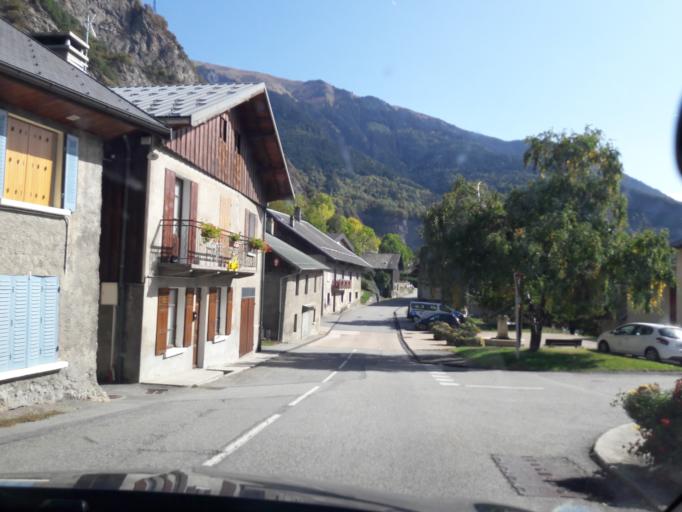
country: FR
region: Rhone-Alpes
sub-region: Departement de la Savoie
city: Saint-Jean-de-Maurienne
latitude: 45.3080
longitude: 6.3569
